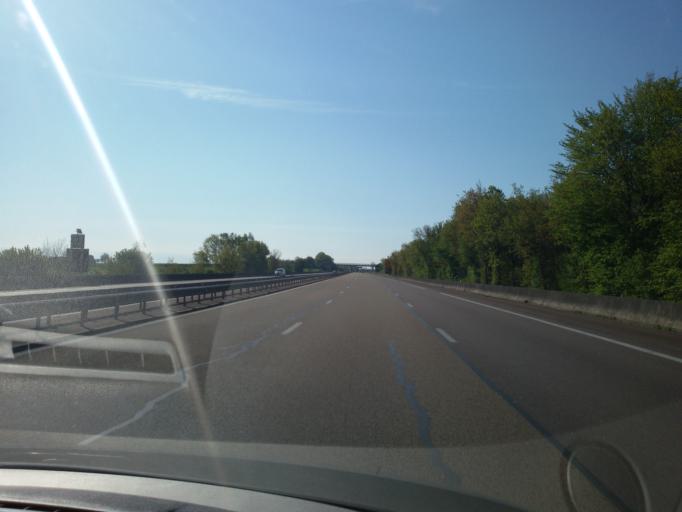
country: FR
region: Bourgogne
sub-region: Departement de l'Yonne
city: Saint-Julien-du-Sault
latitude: 47.9688
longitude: 3.2055
